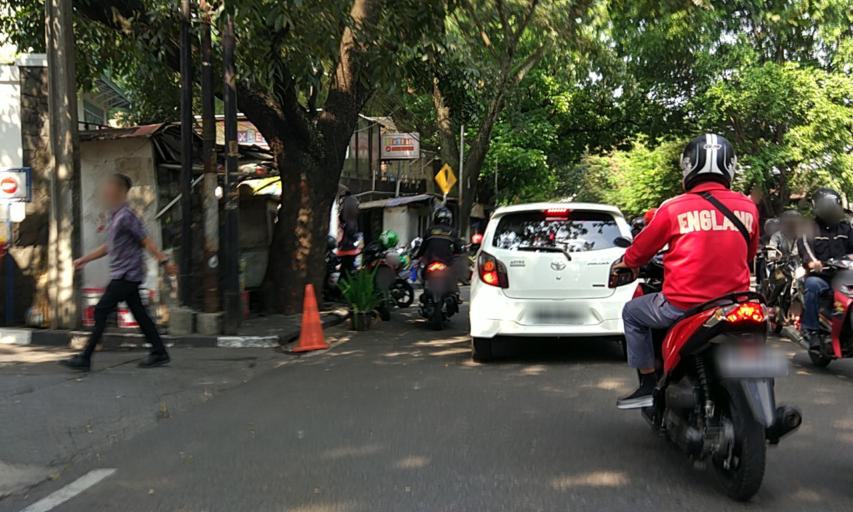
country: ID
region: West Java
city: Bandung
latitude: -6.9036
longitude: 107.6085
